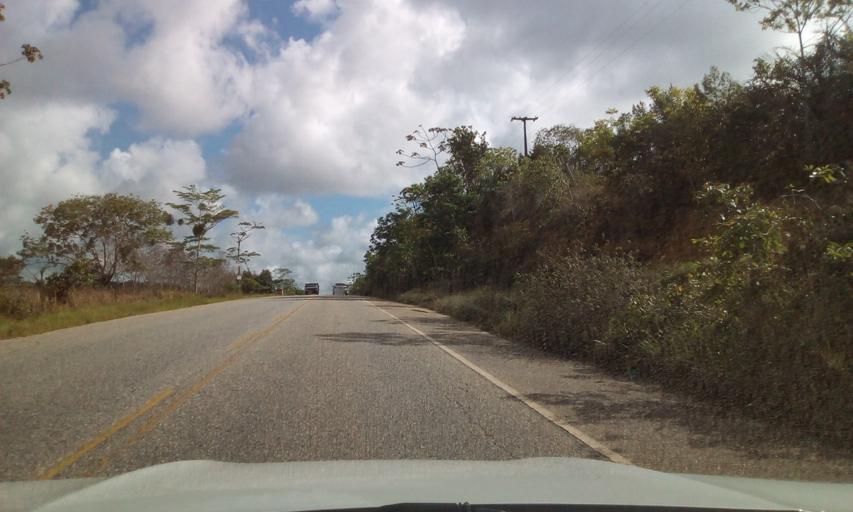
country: BR
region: Sergipe
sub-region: Indiaroba
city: Indiaroba
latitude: -11.4055
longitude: -37.4850
